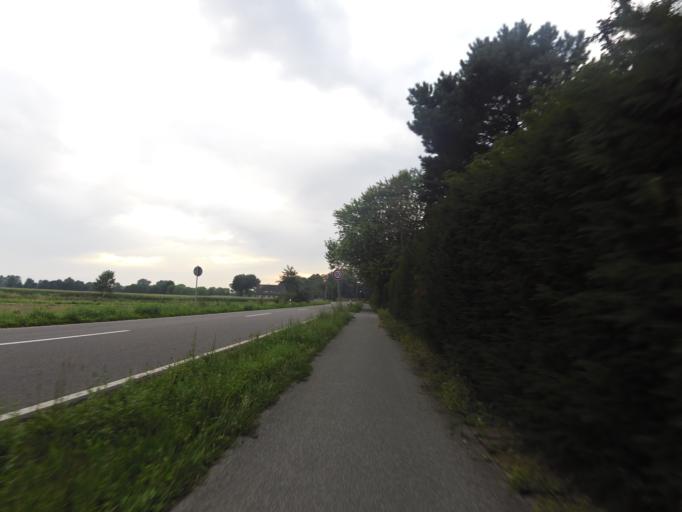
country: NL
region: Gelderland
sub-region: Oude IJsselstreek
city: Gendringen
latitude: 51.8646
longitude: 6.3912
